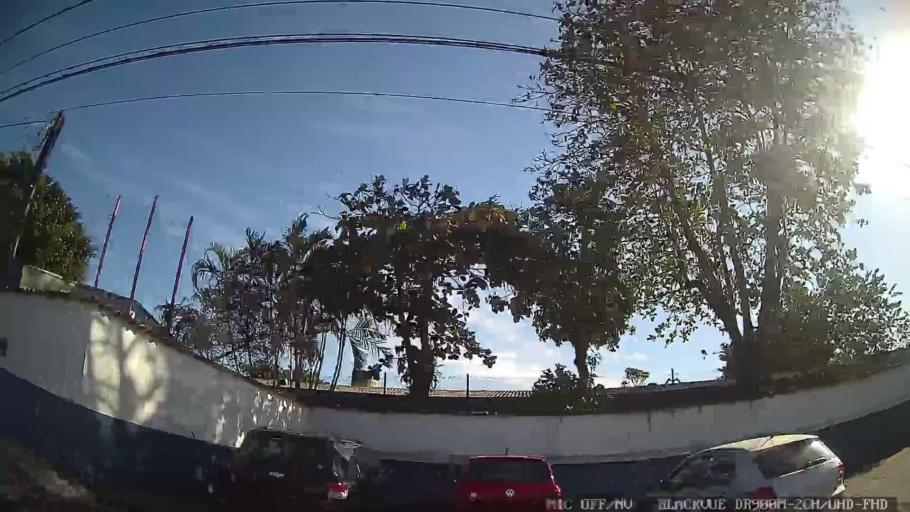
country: BR
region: Sao Paulo
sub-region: Guaruja
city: Guaruja
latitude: -23.9585
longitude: -46.2789
